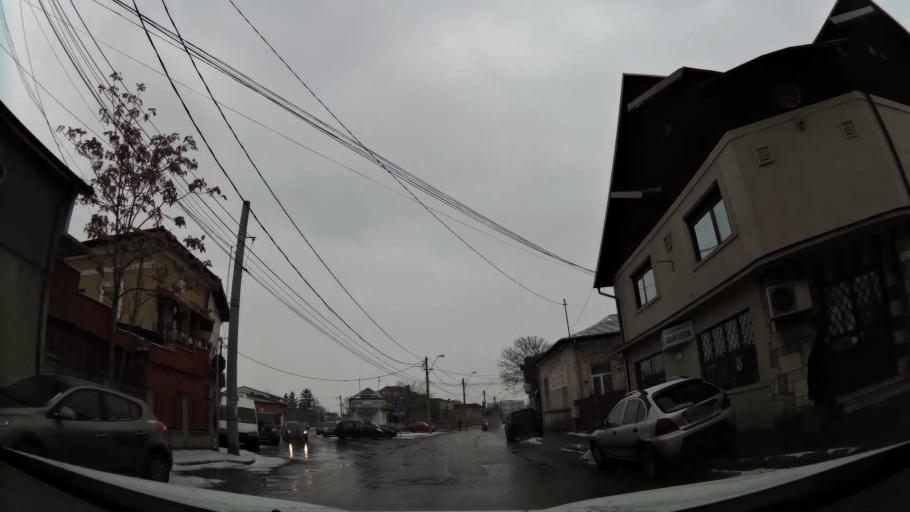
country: RO
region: Prahova
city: Ploiesti
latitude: 44.9477
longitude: 26.0242
